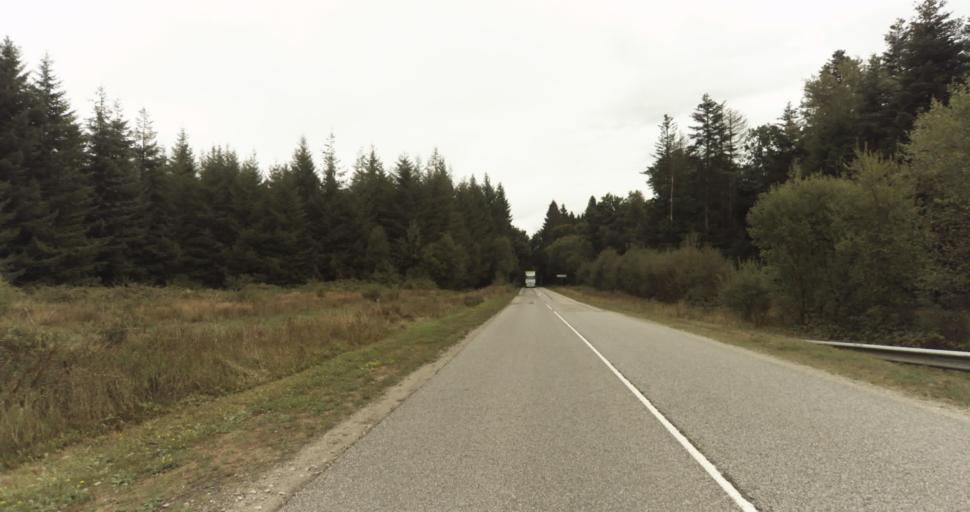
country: FR
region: Lower Normandy
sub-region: Departement de l'Orne
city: Gace
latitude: 48.7956
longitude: 0.3385
